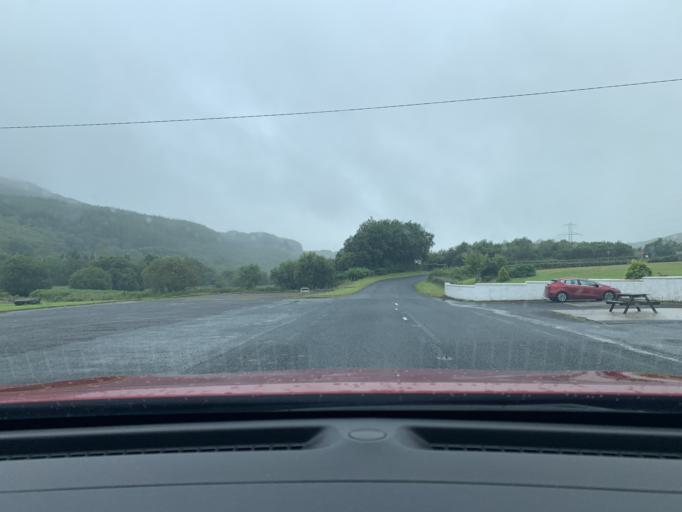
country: IE
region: Ulster
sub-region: County Donegal
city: Donegal
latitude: 54.7094
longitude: -7.9705
